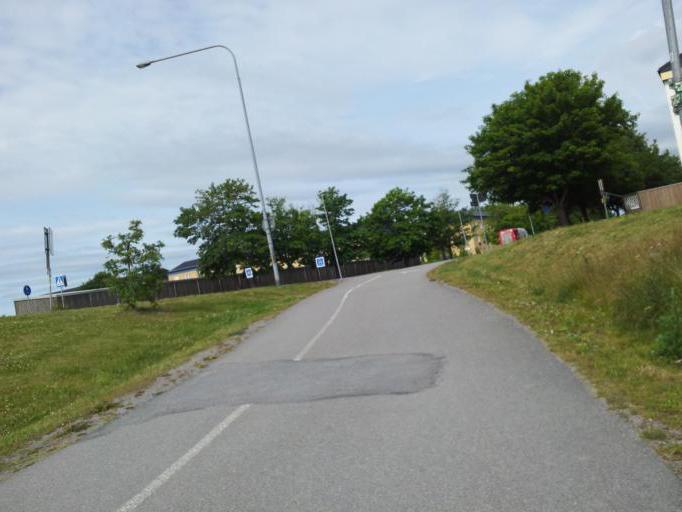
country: SE
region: Uppsala
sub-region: Uppsala Kommun
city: Gamla Uppsala
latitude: 59.8860
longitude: 17.6573
